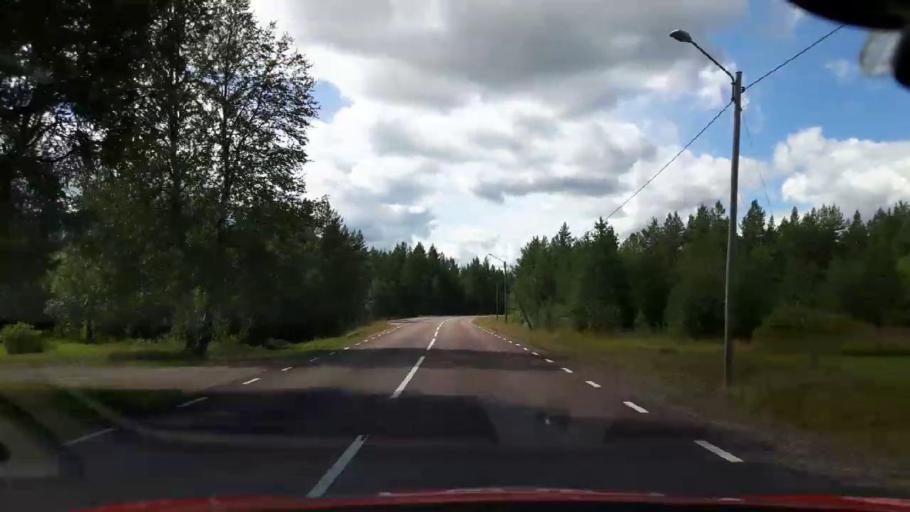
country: SE
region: Jaemtland
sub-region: Harjedalens Kommun
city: Sveg
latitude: 61.8623
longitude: 14.1100
